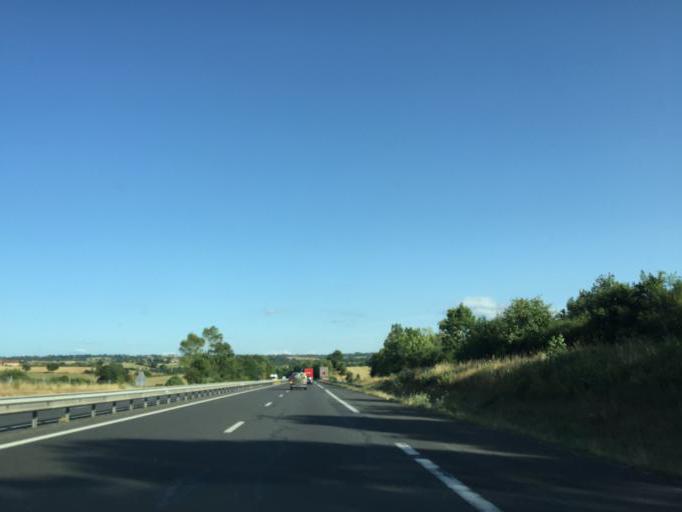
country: FR
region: Auvergne
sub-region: Departement de l'Allier
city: Montmarault
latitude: 46.3374
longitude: 2.8851
